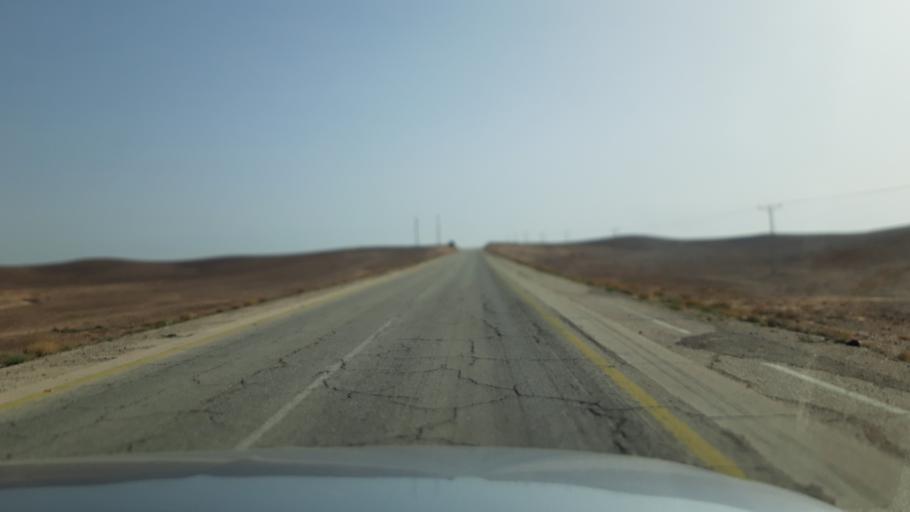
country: JO
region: Amman
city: Al Azraq ash Shamali
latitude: 31.8495
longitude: 36.6685
